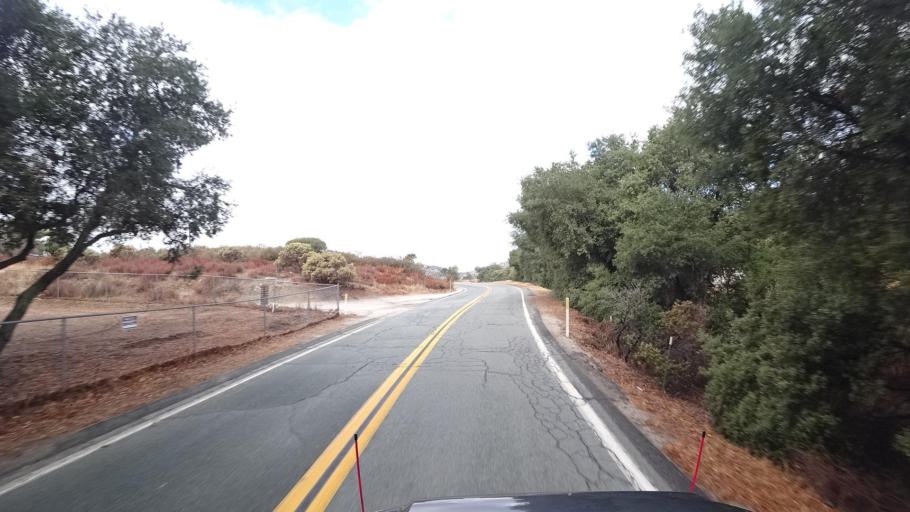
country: MX
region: Baja California
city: Tecate
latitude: 32.6262
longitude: -116.6003
